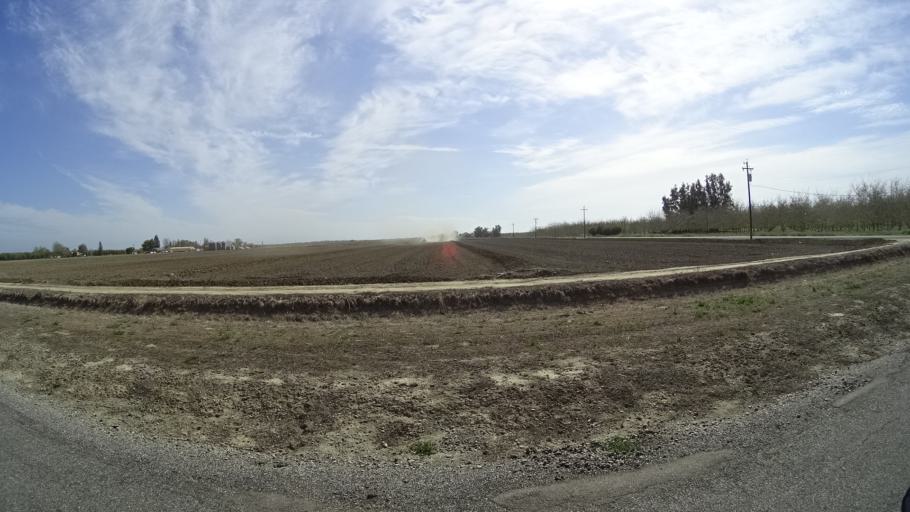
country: US
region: California
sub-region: Glenn County
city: Hamilton City
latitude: 39.6255
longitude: -122.0460
